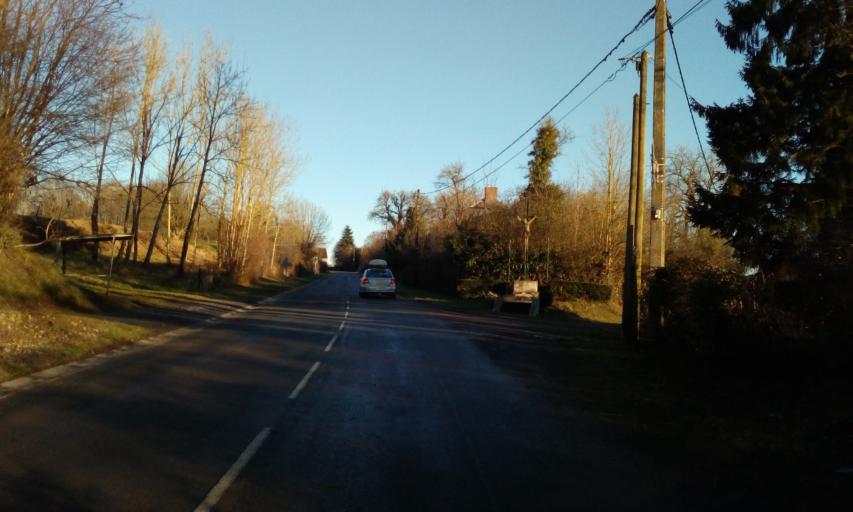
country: FR
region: Picardie
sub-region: Departement de l'Aisne
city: Rozoy-sur-Serre
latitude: 49.7081
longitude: 4.2204
